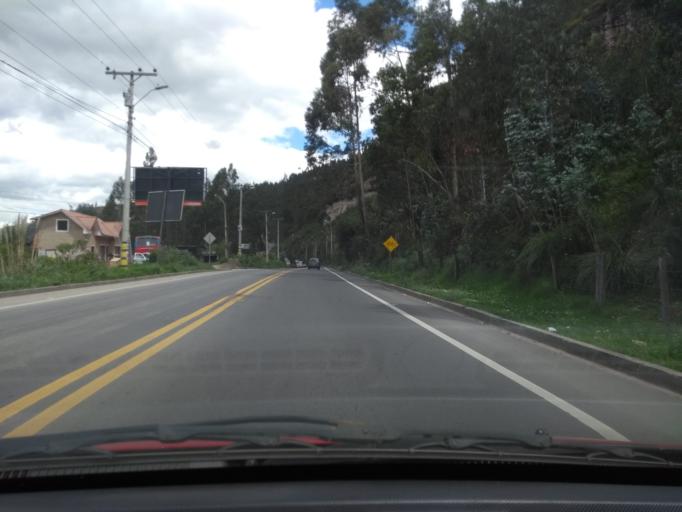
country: EC
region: Azuay
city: Cuenca
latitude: -2.9518
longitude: -79.0482
